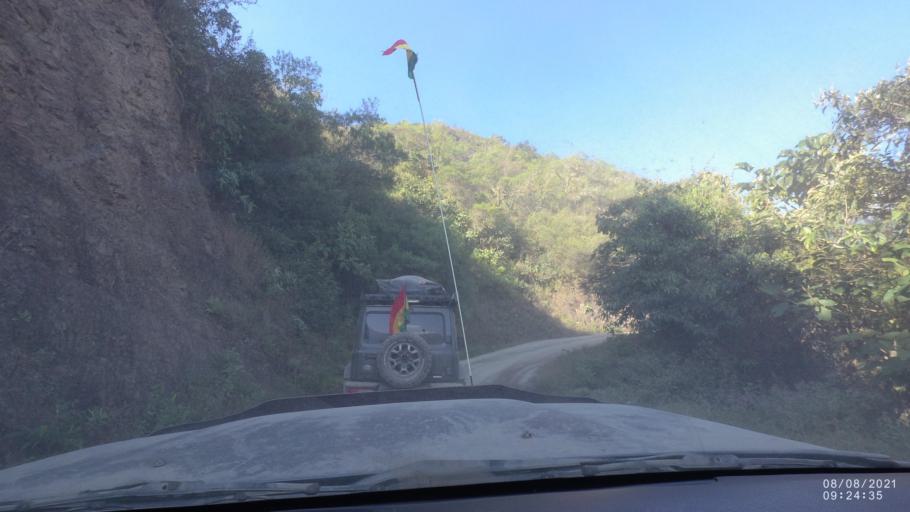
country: BO
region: La Paz
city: Quime
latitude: -16.5789
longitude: -66.7214
